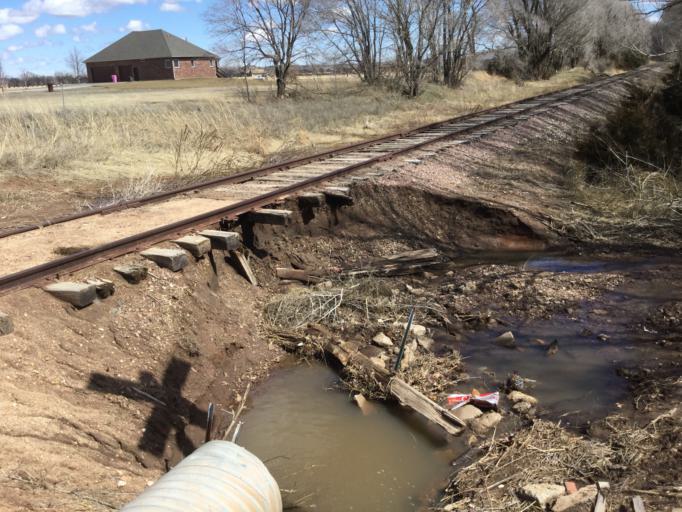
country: US
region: Kansas
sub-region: Sedgwick County
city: Cheney
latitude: 37.6278
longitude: -97.7716
